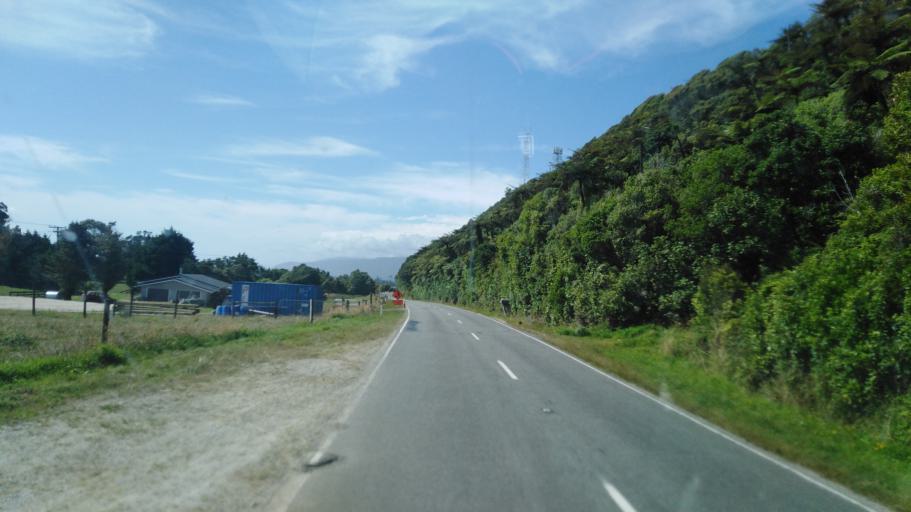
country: NZ
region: West Coast
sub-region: Buller District
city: Westport
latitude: -41.2598
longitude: 172.1127
